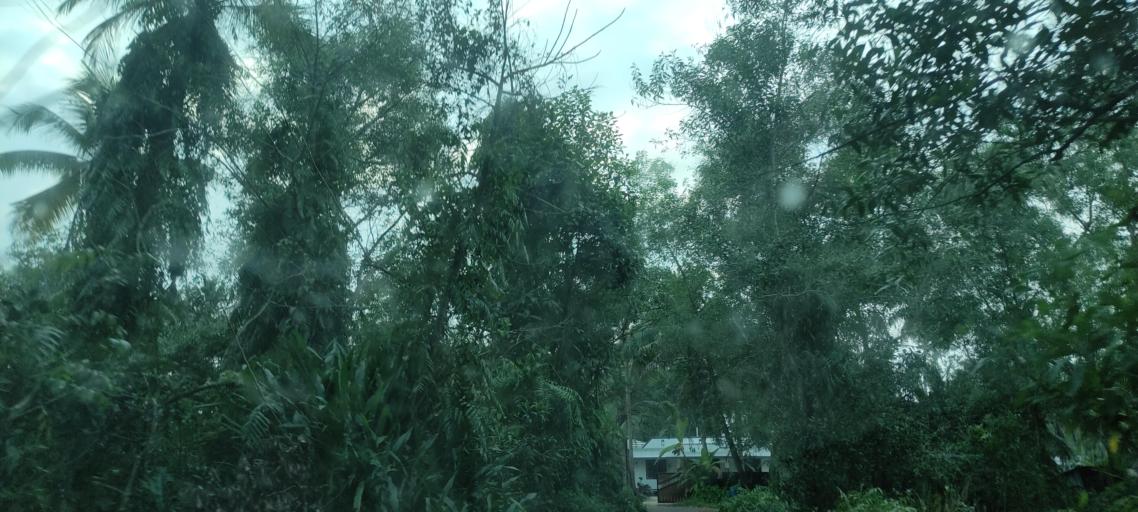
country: IN
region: Kerala
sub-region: Alappuzha
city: Shertallai
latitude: 9.6672
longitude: 76.3577
